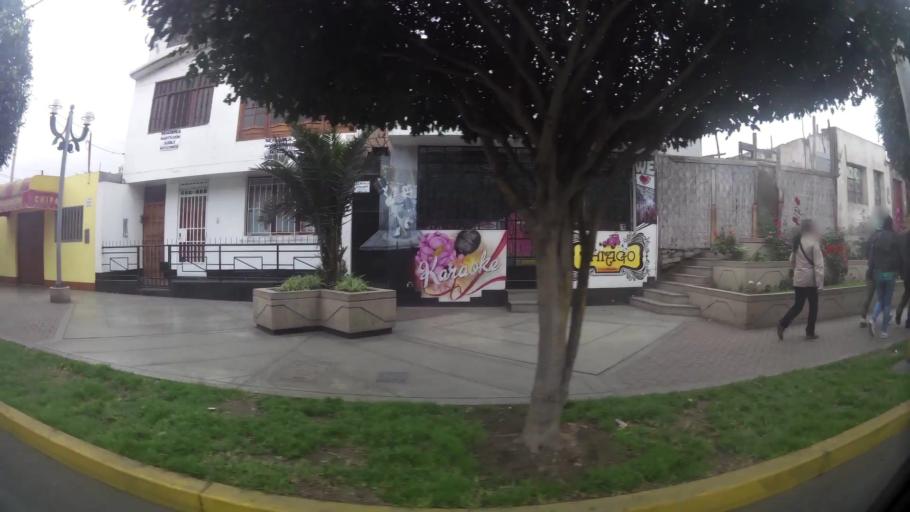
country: PE
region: Lima
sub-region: Provincia de Huaral
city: Chancay
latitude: -11.5618
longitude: -77.2690
